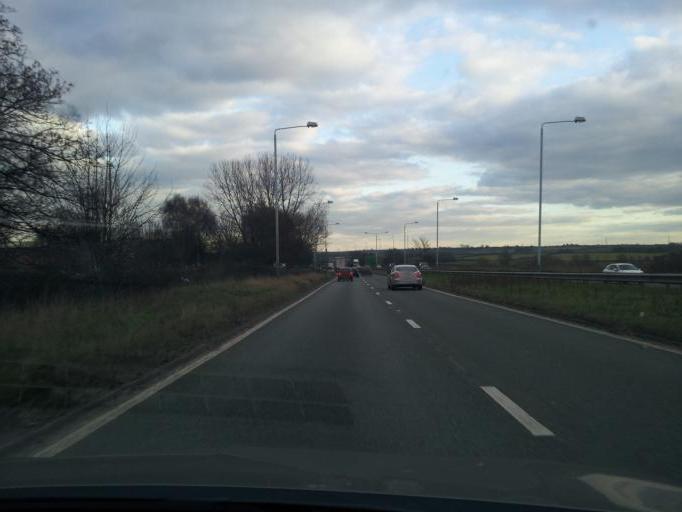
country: GB
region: England
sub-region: Nottinghamshire
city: Ruddington
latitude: 52.9038
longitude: -1.1291
